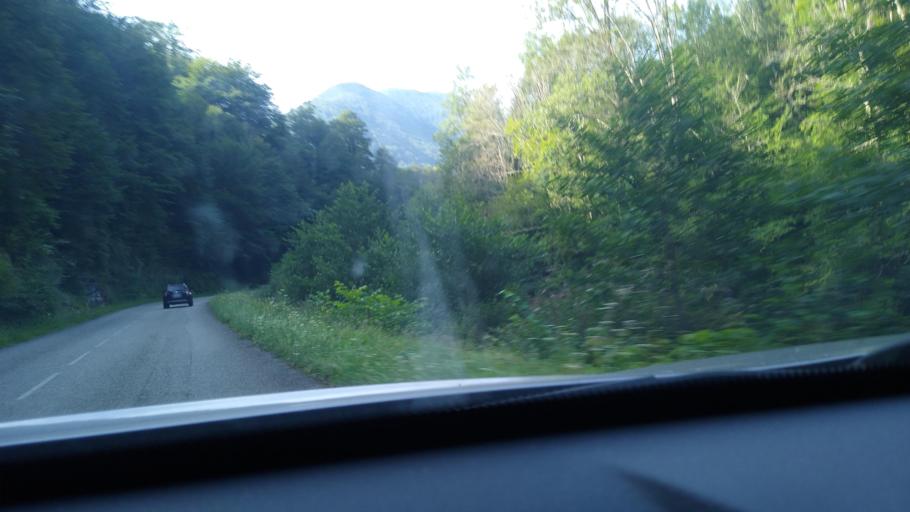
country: FR
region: Midi-Pyrenees
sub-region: Departement de l'Ariege
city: Saint-Girons
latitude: 42.8507
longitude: 1.1928
